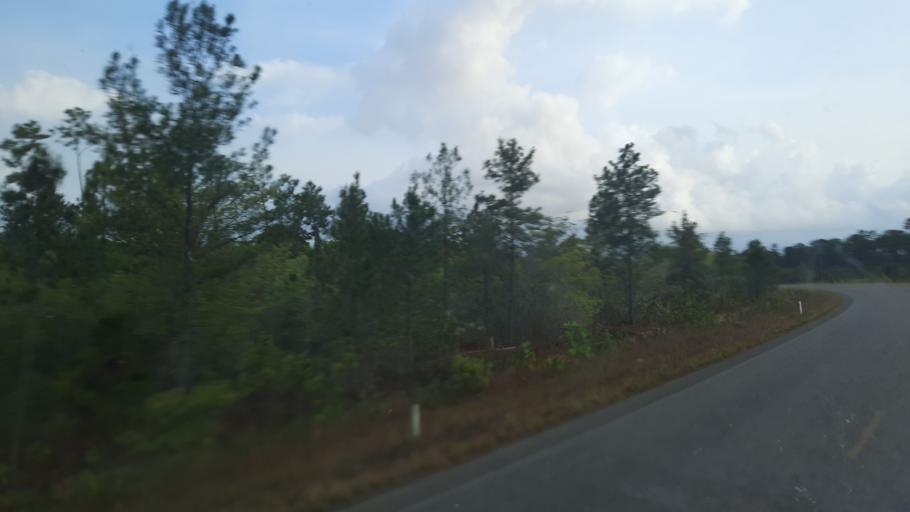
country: BZ
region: Stann Creek
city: Placencia
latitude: 16.6792
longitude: -88.4379
